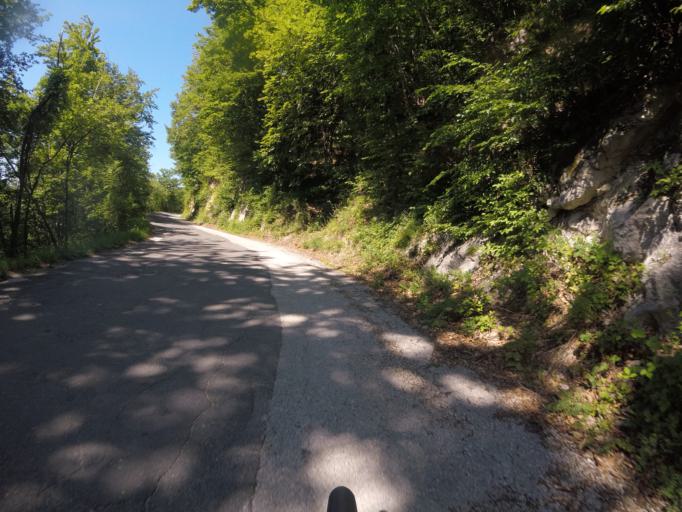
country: SI
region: Brezice
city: Brezice
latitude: 45.8338
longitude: 15.5638
